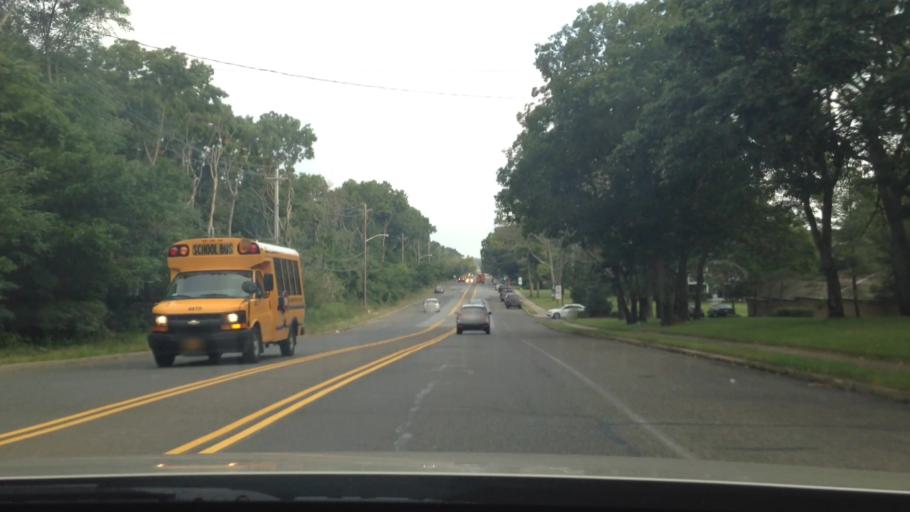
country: US
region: New York
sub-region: Suffolk County
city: Selden
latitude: 40.8519
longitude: -73.0457
